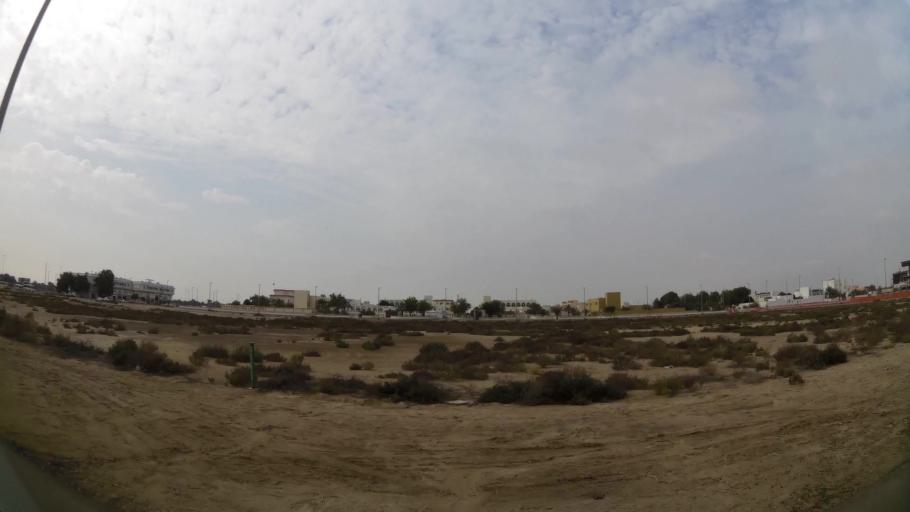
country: AE
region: Abu Dhabi
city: Abu Dhabi
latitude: 24.6391
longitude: 54.7269
